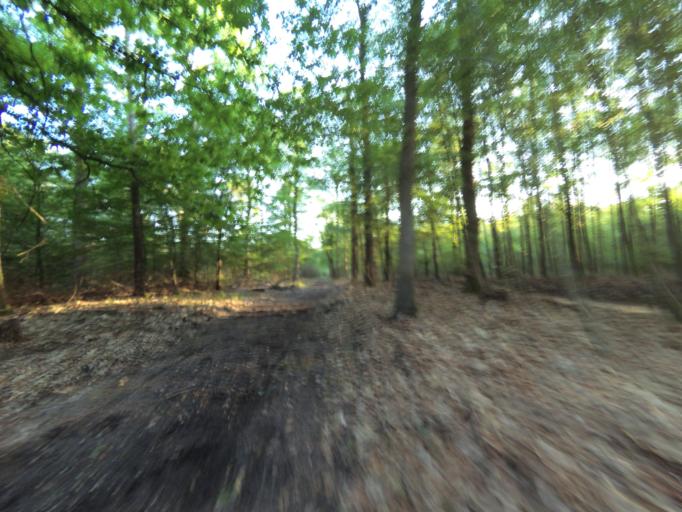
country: NL
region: Gelderland
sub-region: Gemeente Apeldoorn
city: Beekbergen
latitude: 52.1593
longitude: 5.8913
